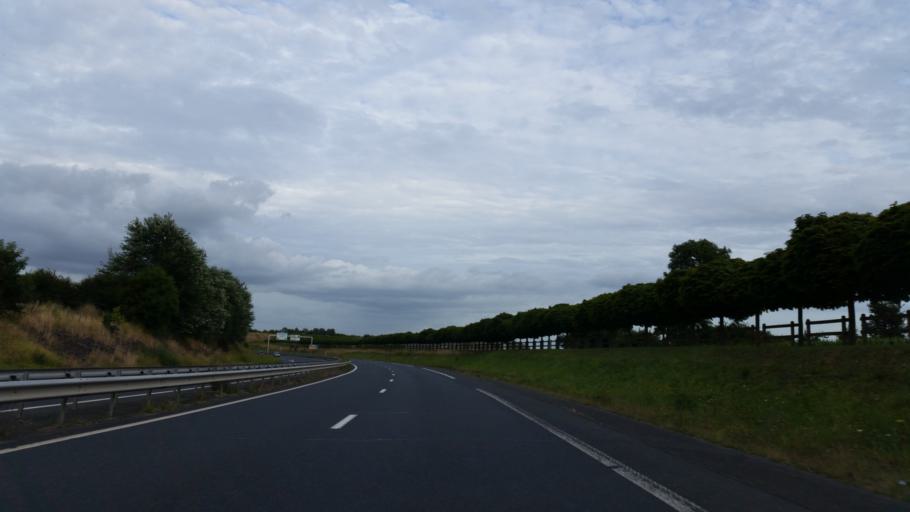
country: FR
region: Lower Normandy
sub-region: Departement du Calvados
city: Grandcamp-Maisy
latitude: 49.3400
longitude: -1.0149
